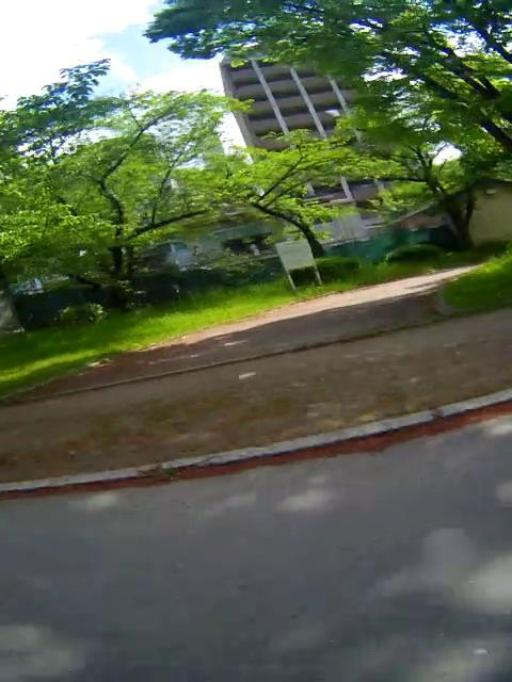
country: JP
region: Osaka
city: Osaka-shi
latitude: 34.7057
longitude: 135.5193
